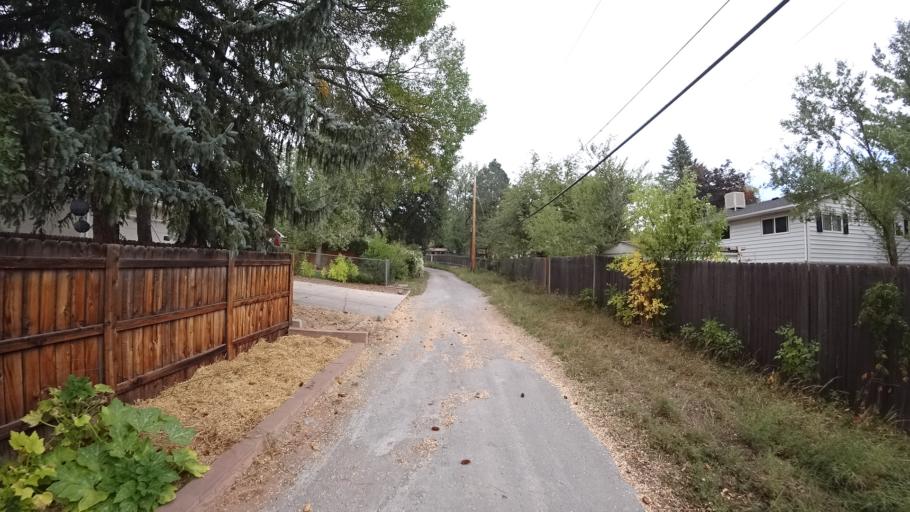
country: US
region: Colorado
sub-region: El Paso County
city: Colorado Springs
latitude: 38.8686
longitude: -104.7804
